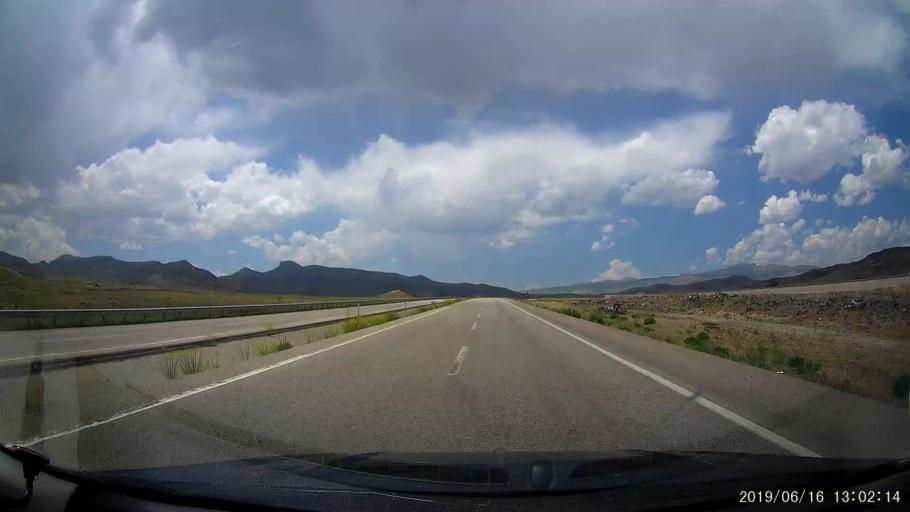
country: TR
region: Agri
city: Sulucem
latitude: 39.5734
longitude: 43.8214
